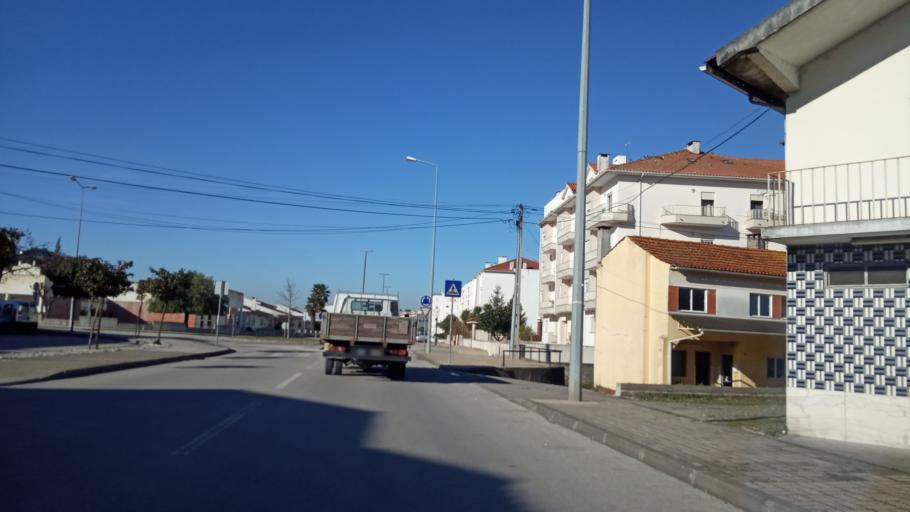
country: PT
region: Aveiro
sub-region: Anadia
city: Anadia
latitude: 40.4408
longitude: -8.4331
